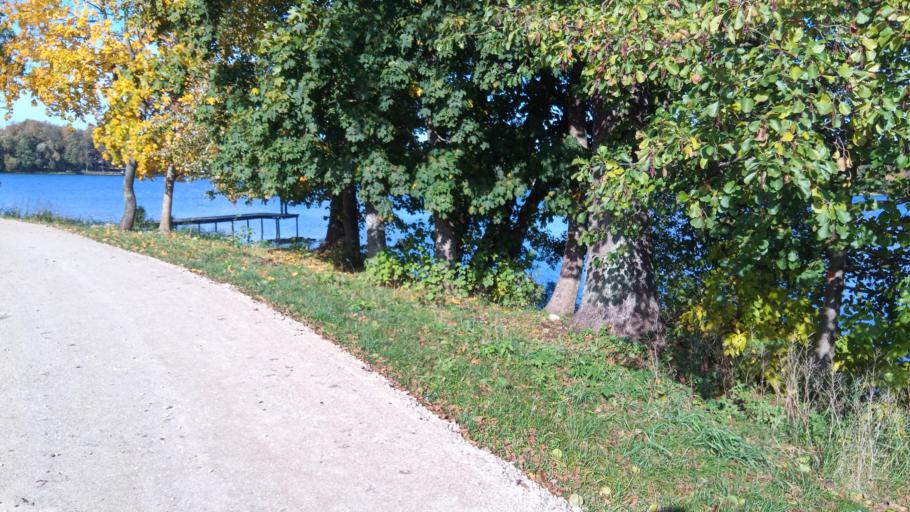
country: LT
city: Trakai
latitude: 54.6407
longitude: 24.9388
